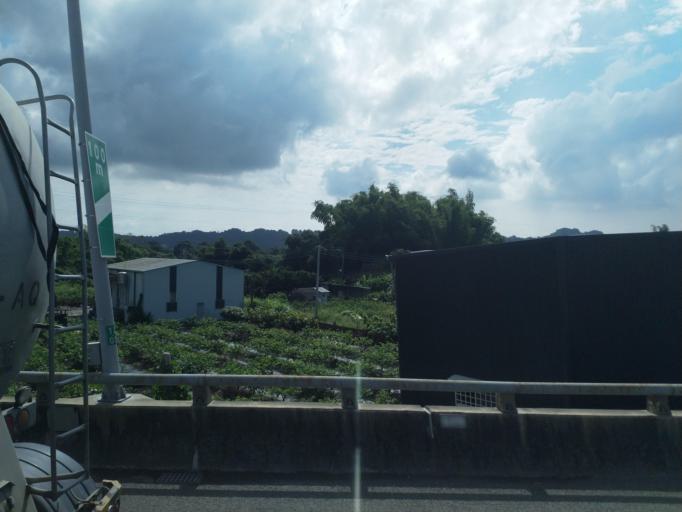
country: TW
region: Taiwan
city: Fengshan
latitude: 22.7520
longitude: 120.3659
